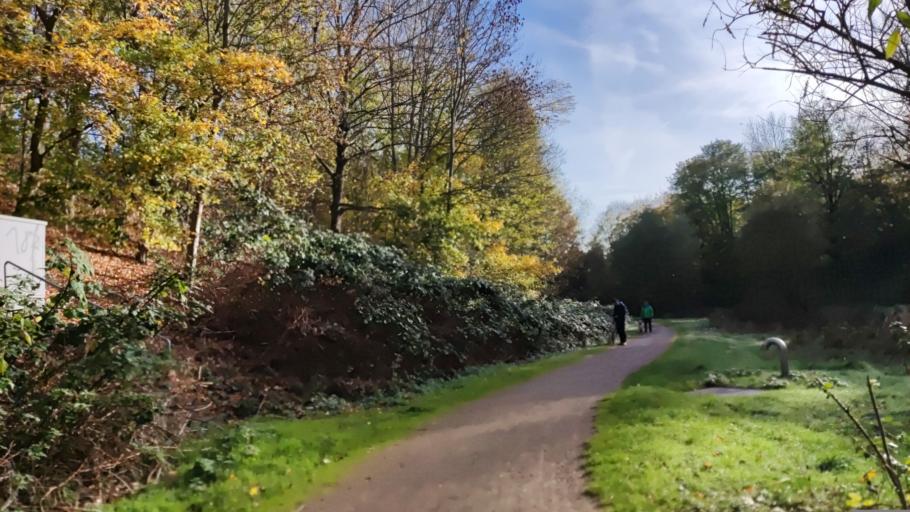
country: DE
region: North Rhine-Westphalia
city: Bochum-Hordel
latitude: 51.5251
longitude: 7.1946
